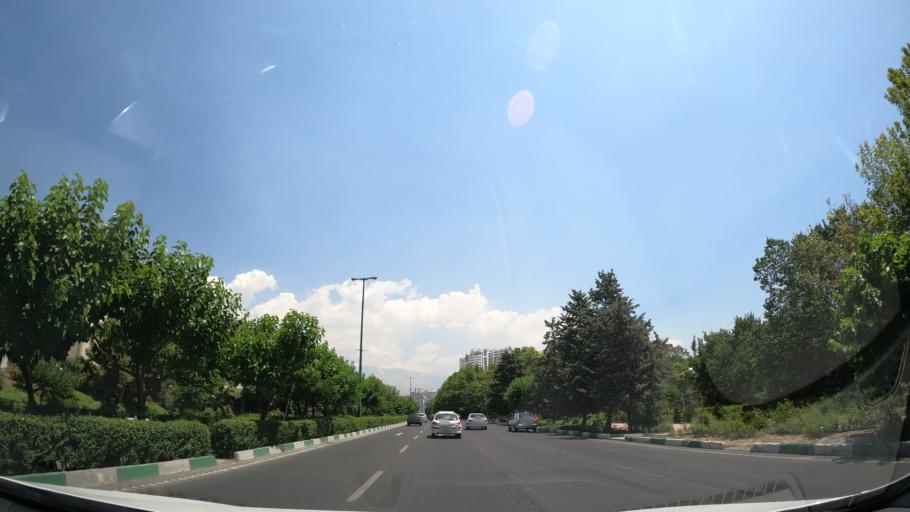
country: IR
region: Tehran
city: Tajrish
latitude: 35.7636
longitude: 51.3769
